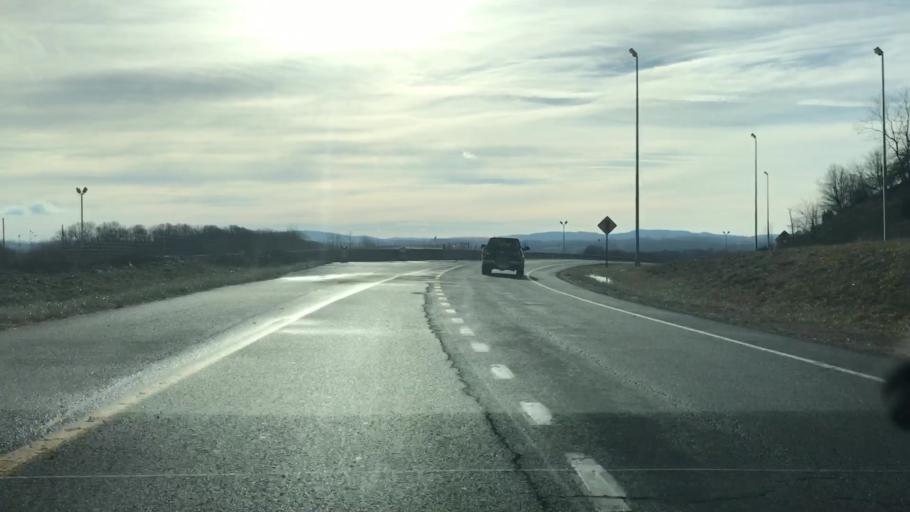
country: US
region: Virginia
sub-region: Montgomery County
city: Merrimac
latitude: 37.1901
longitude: -80.4018
